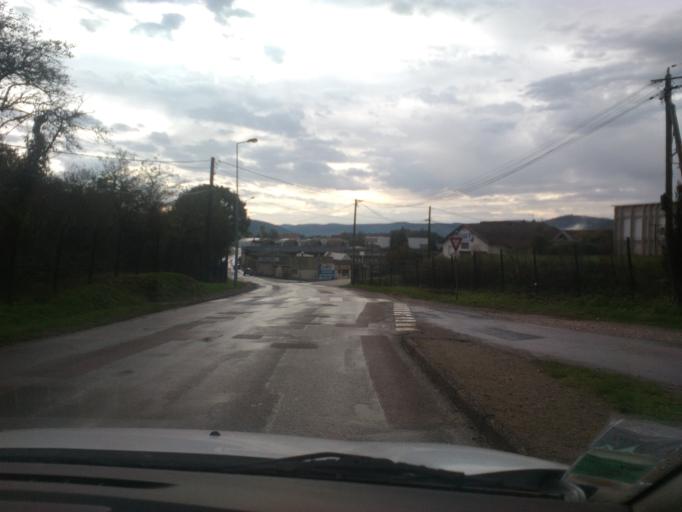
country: FR
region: Lorraine
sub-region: Departement des Vosges
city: Bruyeres
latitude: 48.2050
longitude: 6.7177
